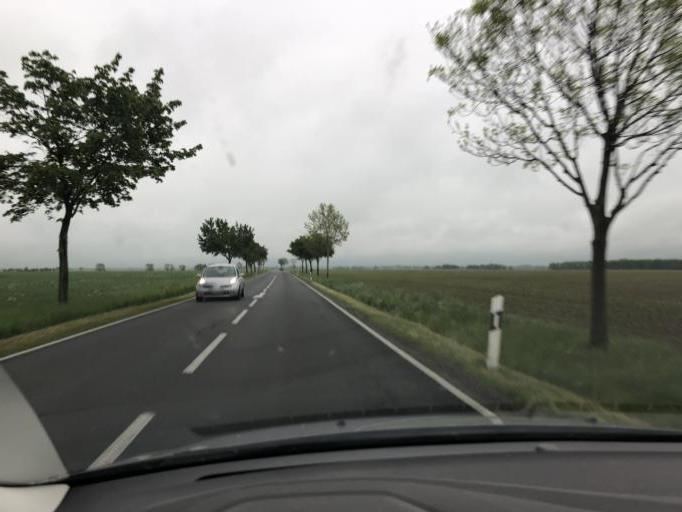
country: DE
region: Saxony
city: Zschortau
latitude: 51.5013
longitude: 12.3867
